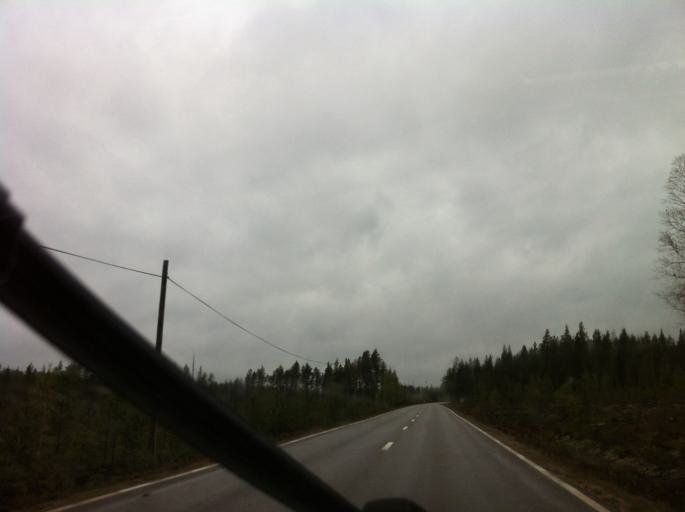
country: SE
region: Jaemtland
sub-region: Harjedalens Kommun
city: Sveg
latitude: 62.1465
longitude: 13.9310
